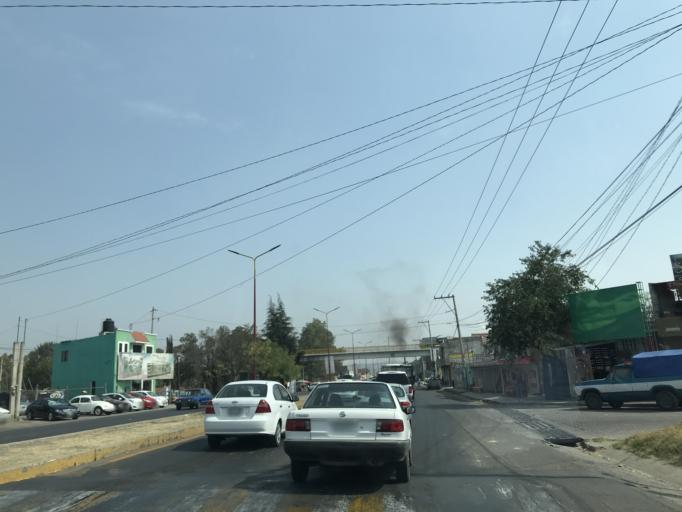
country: MX
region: Tlaxcala
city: La Magdalena Tlaltelulco
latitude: 19.2907
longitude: -98.1951
